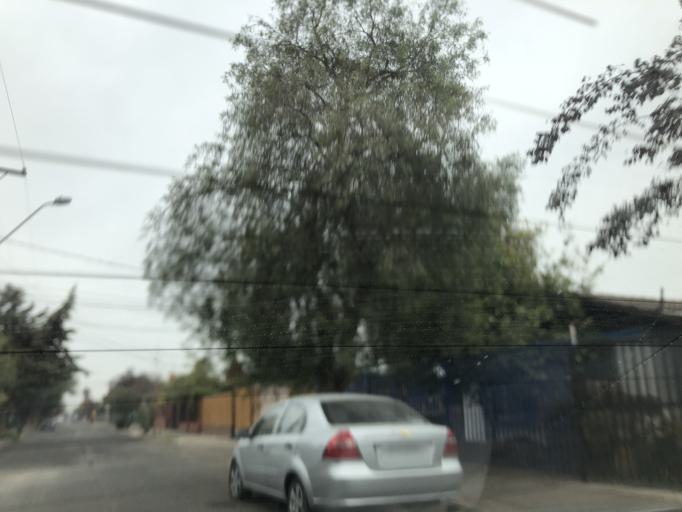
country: CL
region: Santiago Metropolitan
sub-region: Provincia de Cordillera
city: Puente Alto
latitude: -33.5889
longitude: -70.5891
